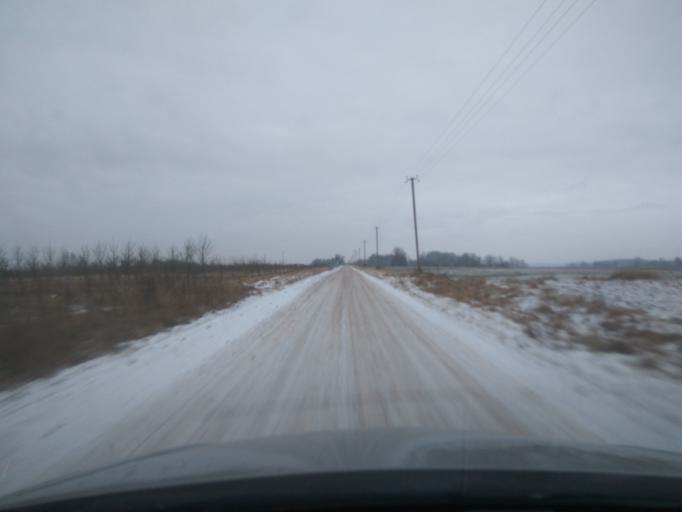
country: LV
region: Aizpute
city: Aizpute
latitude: 56.7647
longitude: 21.7094
